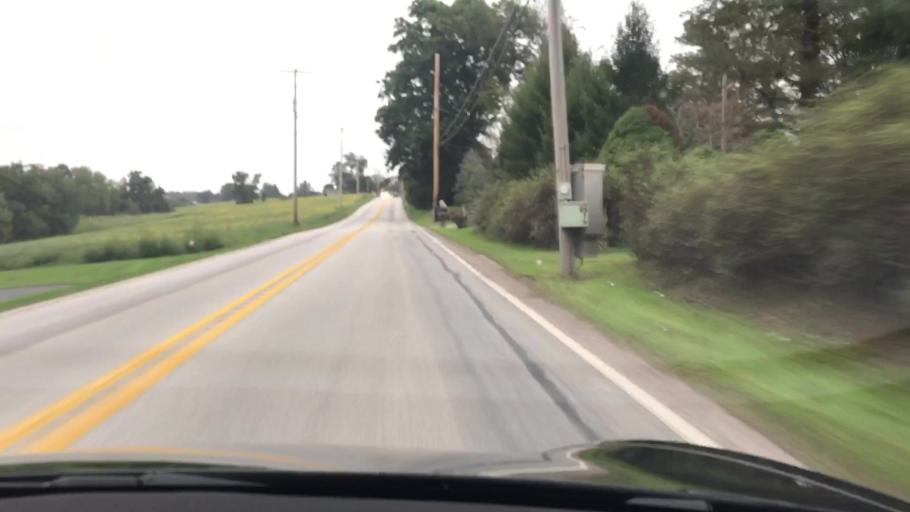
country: US
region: Pennsylvania
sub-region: York County
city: Dover
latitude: 40.0085
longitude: -76.8279
